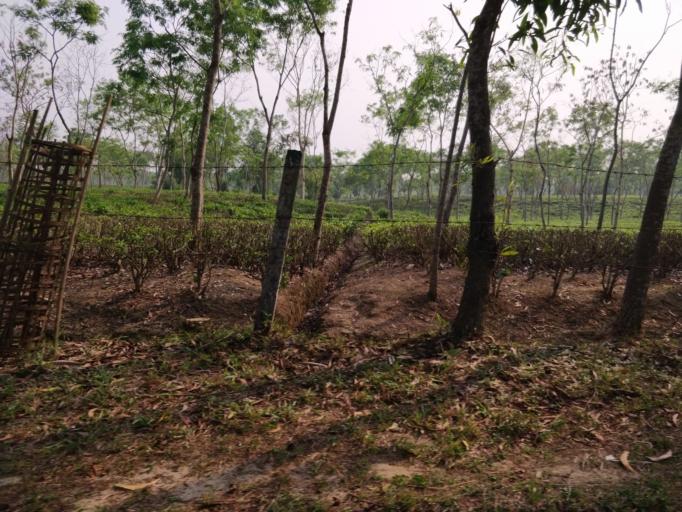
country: IN
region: Tripura
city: Khowai
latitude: 24.1295
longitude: 91.3902
